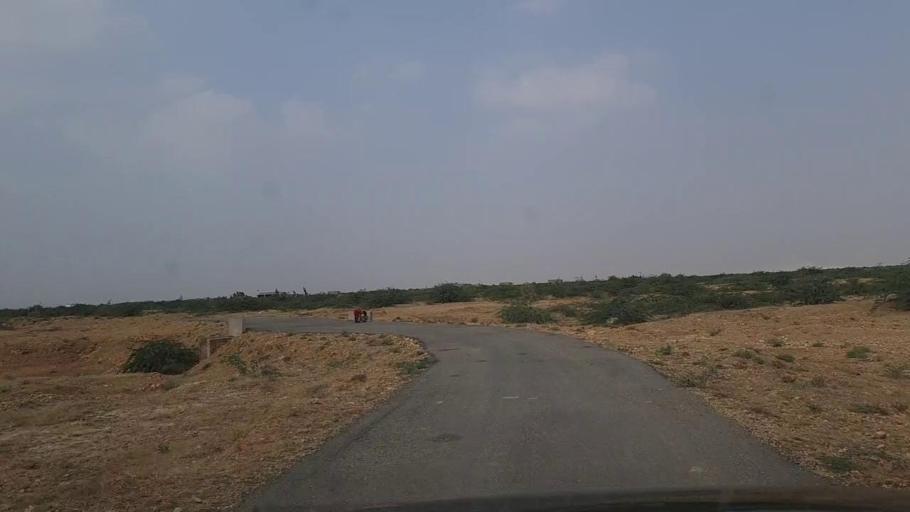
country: PK
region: Sindh
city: Thatta
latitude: 24.8067
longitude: 67.9130
